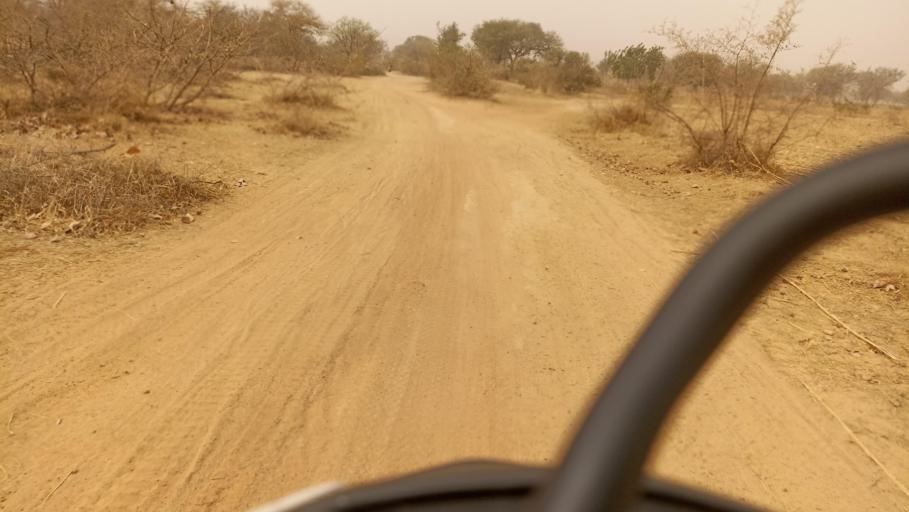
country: BF
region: Nord
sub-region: Province du Zondoma
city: Gourcy
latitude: 13.2796
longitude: -2.5336
